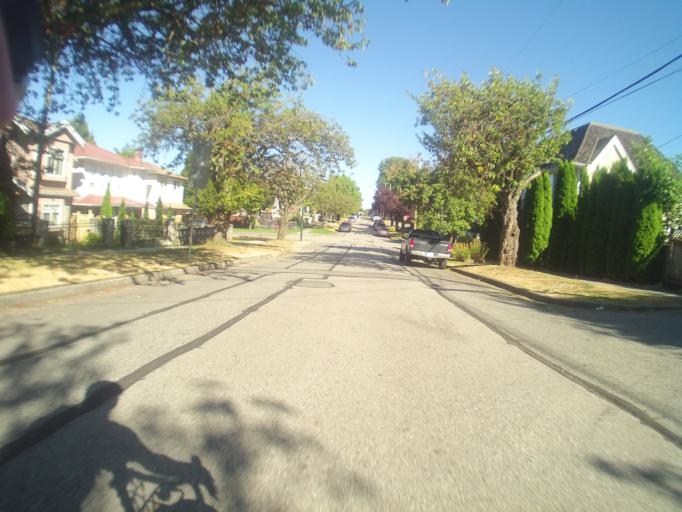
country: CA
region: British Columbia
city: Vancouver
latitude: 49.2446
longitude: -123.0807
